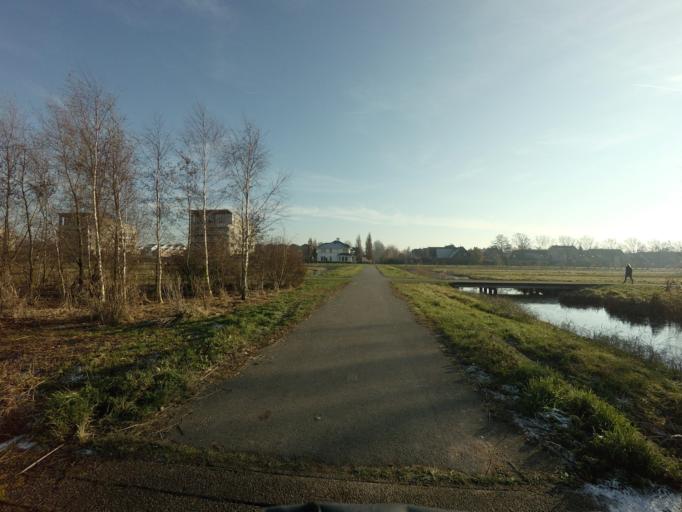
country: NL
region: Utrecht
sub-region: Gemeente De Ronde Venen
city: Mijdrecht
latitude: 52.2074
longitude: 4.8495
